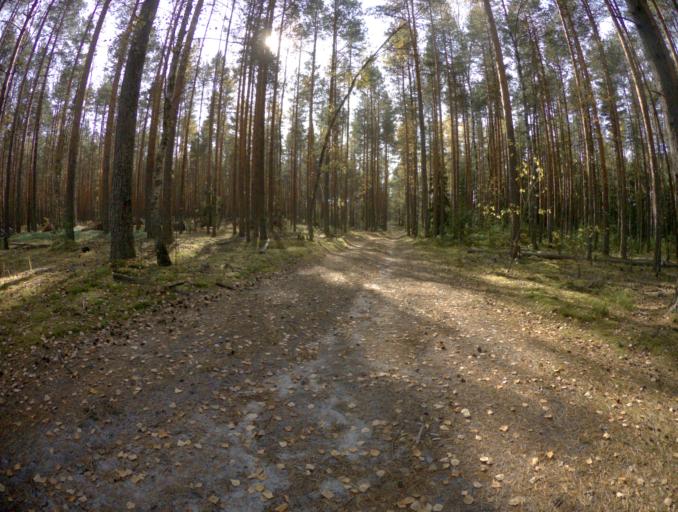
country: RU
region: Vladimir
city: Vorsha
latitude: 55.9391
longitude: 40.1245
